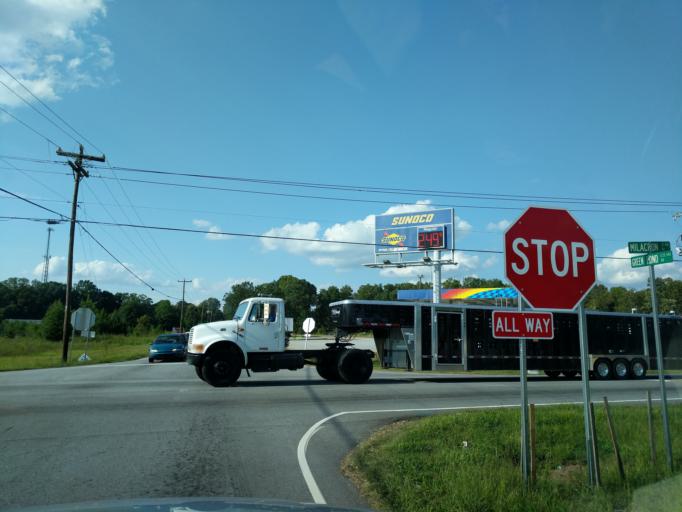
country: US
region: South Carolina
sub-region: Greenville County
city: Fountain Inn
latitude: 34.6739
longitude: -82.2187
